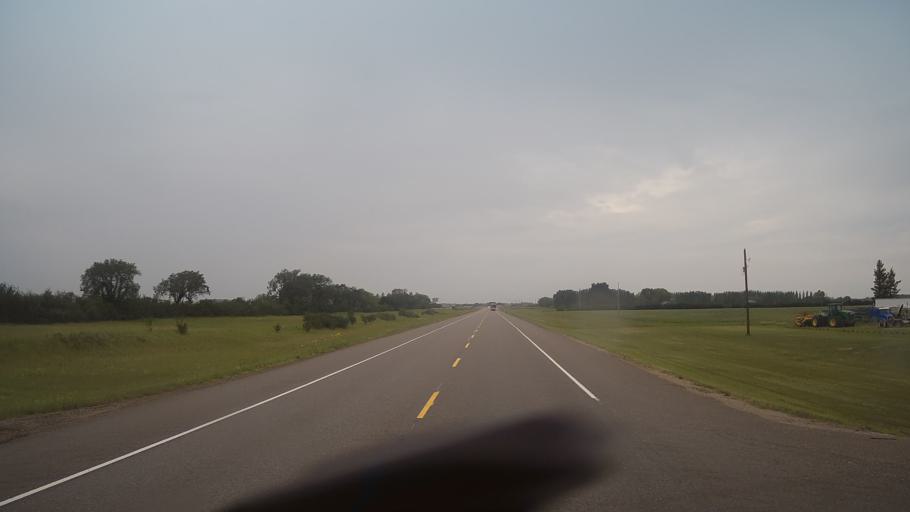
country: CA
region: Saskatchewan
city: Dalmeny
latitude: 52.1292
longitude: -106.8725
